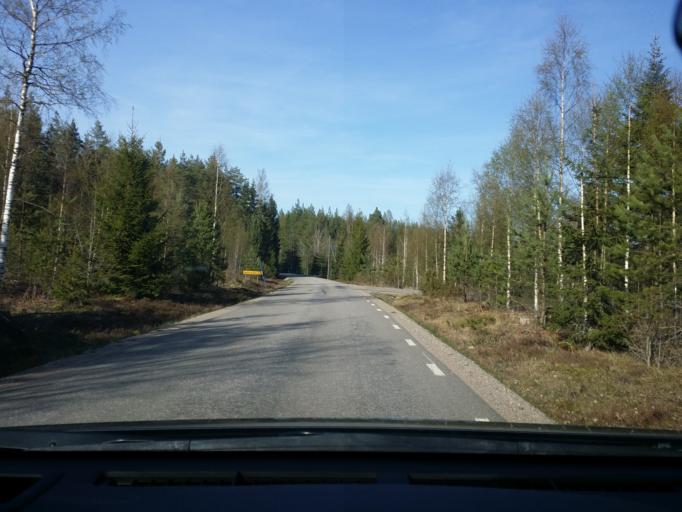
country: SE
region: Dalarna
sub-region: Avesta Kommun
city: Avesta
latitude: 60.0652
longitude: 16.3425
